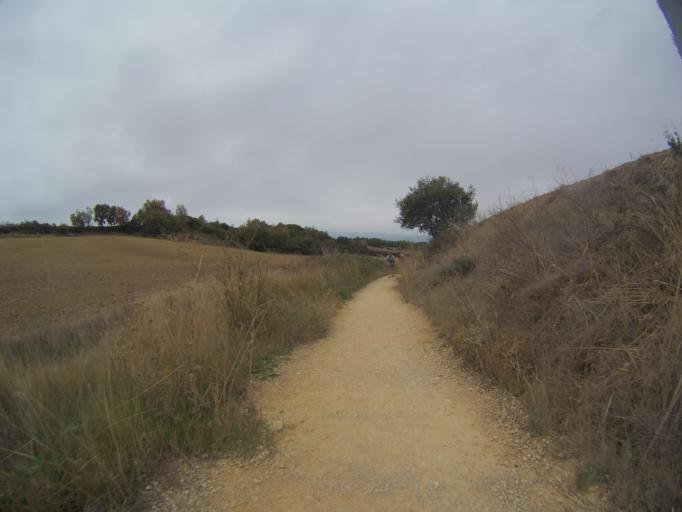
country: ES
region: Navarre
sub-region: Provincia de Navarra
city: Villatuerta
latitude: 42.6649
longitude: -1.9630
